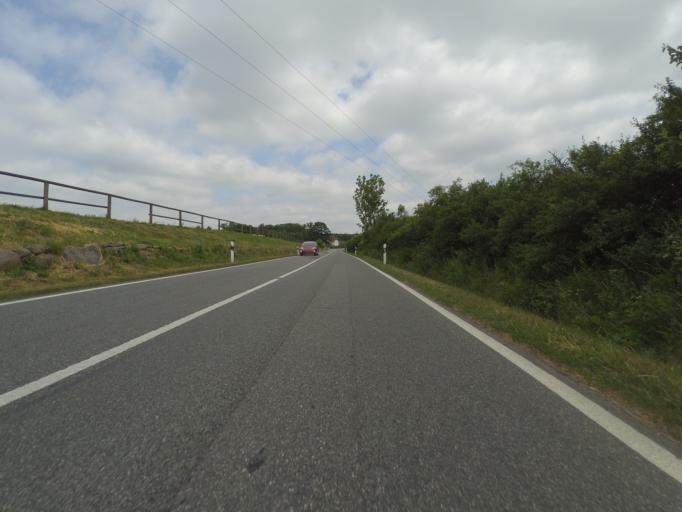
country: DE
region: Mecklenburg-Vorpommern
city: Grabowhofe
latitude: 53.5427
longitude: 12.5480
